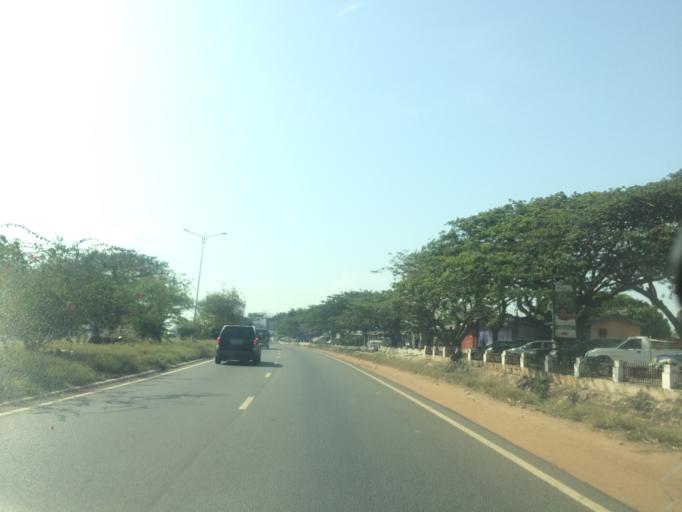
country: GH
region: Greater Accra
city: Accra
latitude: 5.5603
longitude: -0.1692
